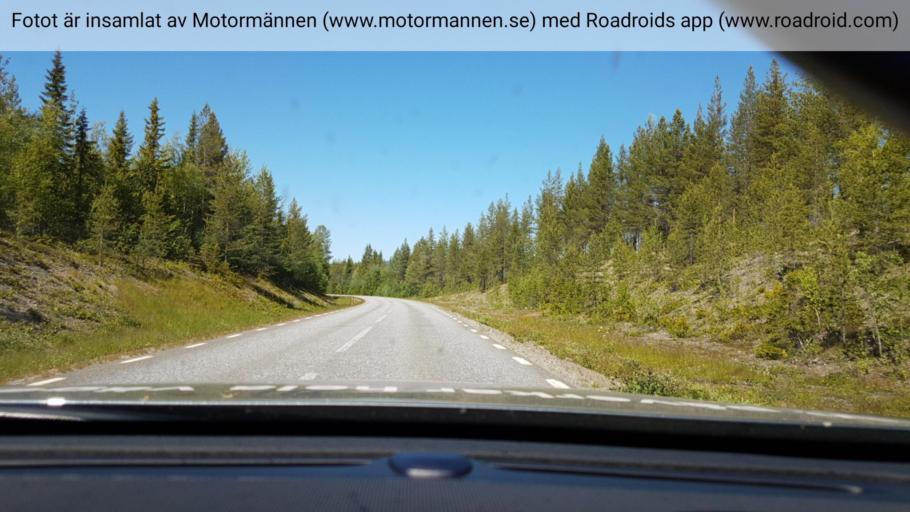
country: SE
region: Vaesterbotten
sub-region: Vilhelmina Kommun
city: Sjoberg
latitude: 64.8674
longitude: 15.8948
